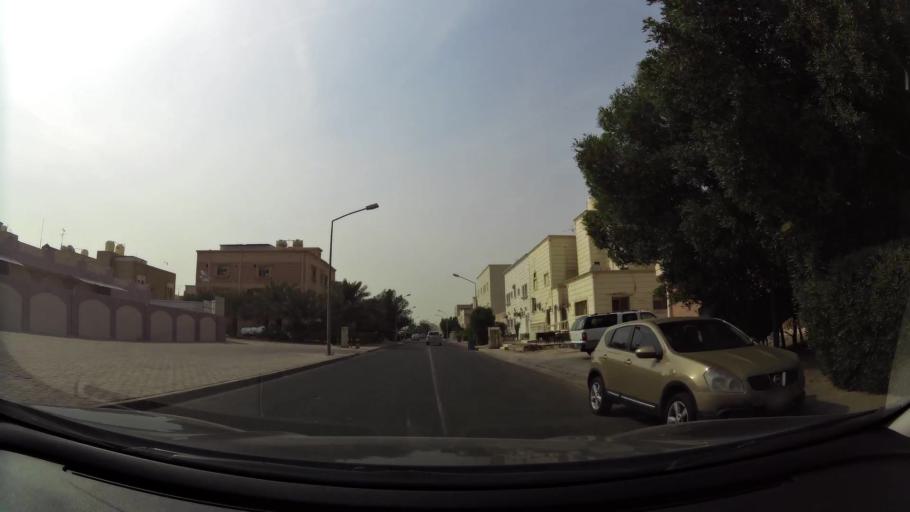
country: KW
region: Al Asimah
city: Ar Rabiyah
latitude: 29.2837
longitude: 47.9430
